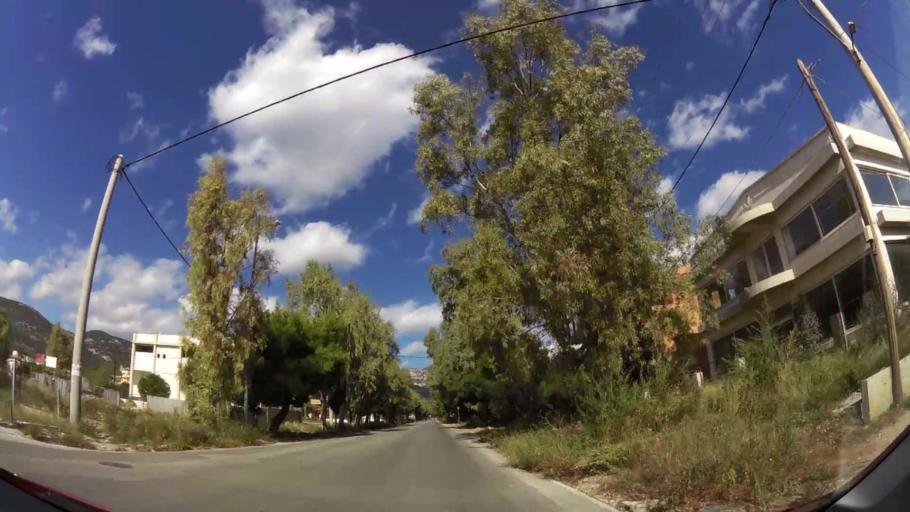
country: GR
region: Attica
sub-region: Nomarchia Anatolikis Attikis
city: Acharnes
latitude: 38.1080
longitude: 23.7358
